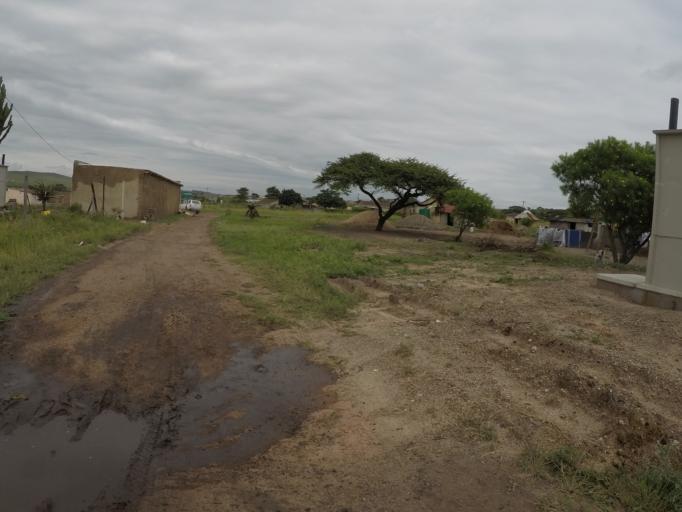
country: ZA
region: KwaZulu-Natal
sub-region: uThungulu District Municipality
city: Empangeni
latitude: -28.7109
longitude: 31.8622
